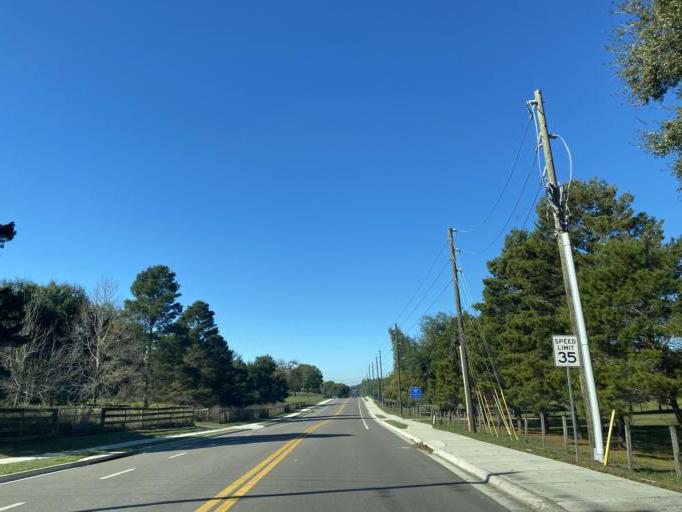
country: US
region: Florida
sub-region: Lake County
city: Minneola
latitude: 28.5251
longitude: -81.7077
